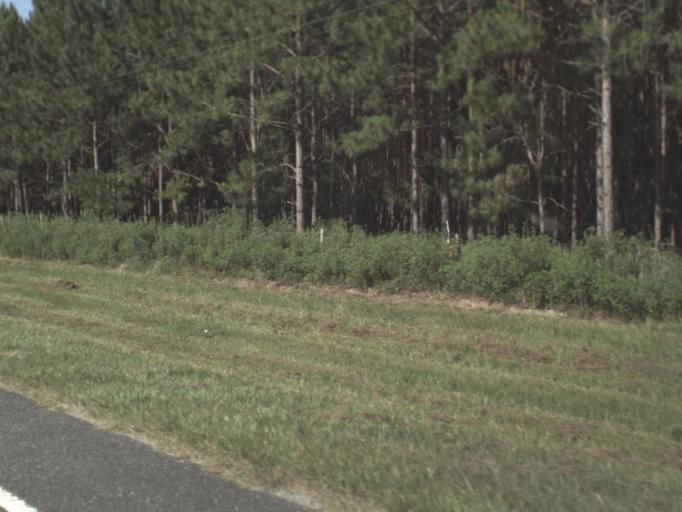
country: US
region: Florida
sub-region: Columbia County
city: Lake City
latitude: 30.0214
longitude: -82.7103
